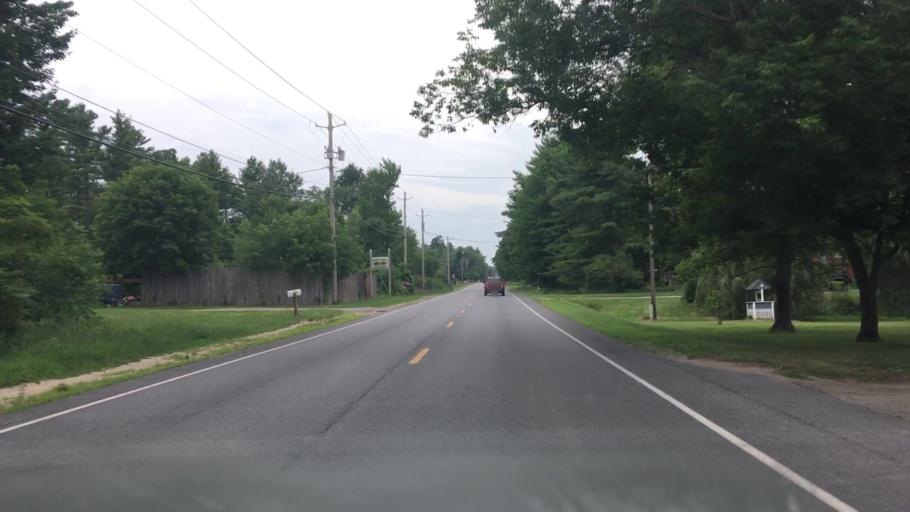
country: US
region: New York
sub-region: Clinton County
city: Plattsburgh West
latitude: 44.6581
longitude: -73.5102
